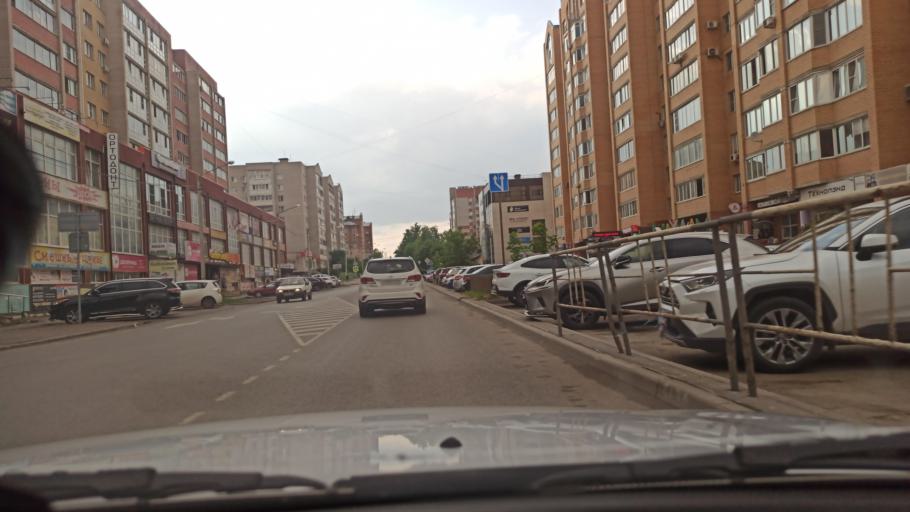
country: RU
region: Vologda
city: Vologda
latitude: 59.2094
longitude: 39.8433
